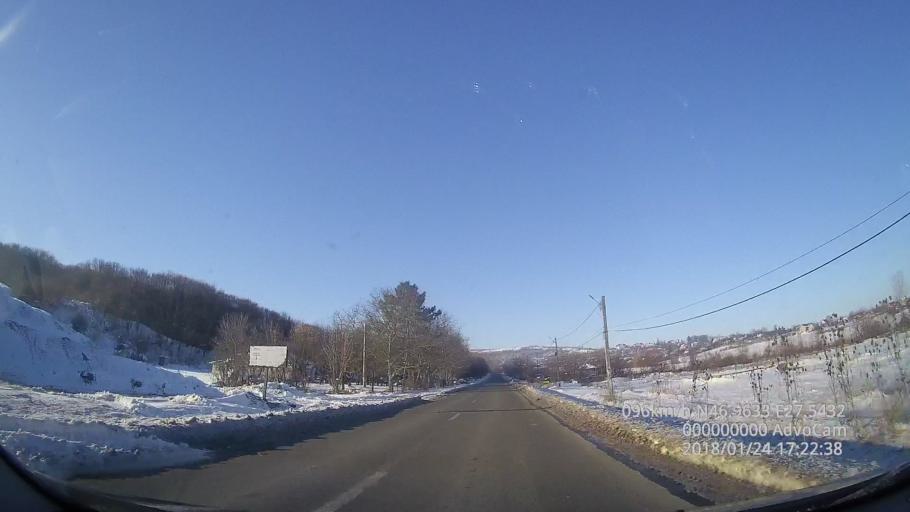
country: RO
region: Iasi
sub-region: Comuna Grajduri
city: Grajduri
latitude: 46.9640
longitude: 27.5425
